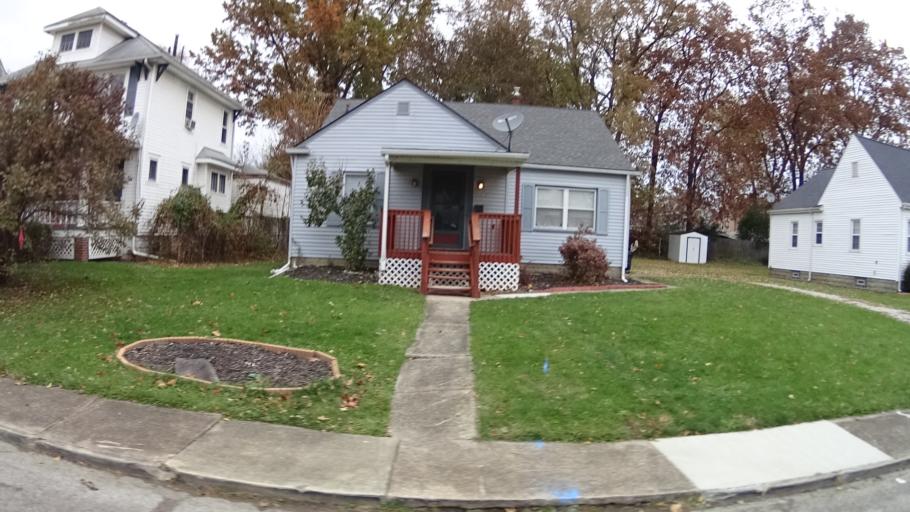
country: US
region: Ohio
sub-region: Lorain County
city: Elyria
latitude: 41.3544
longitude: -82.1061
